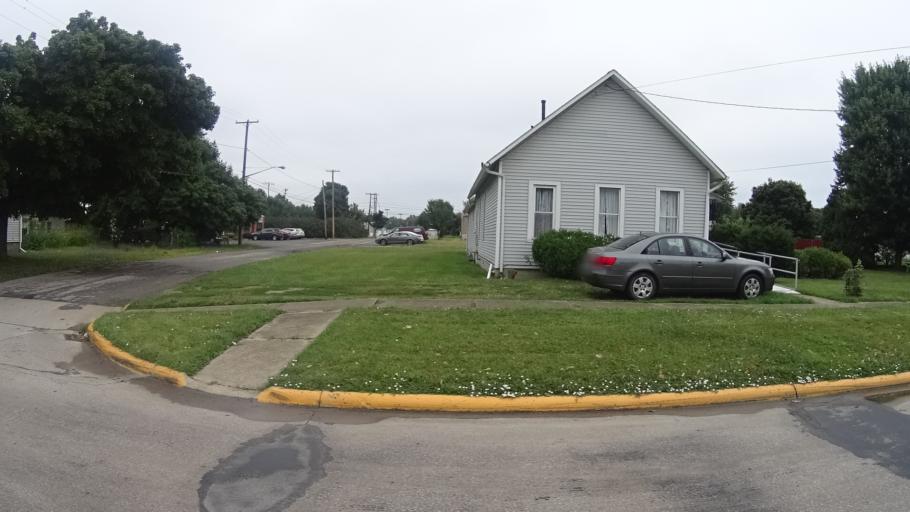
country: US
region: Ohio
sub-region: Erie County
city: Sandusky
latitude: 41.4407
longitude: -82.6987
